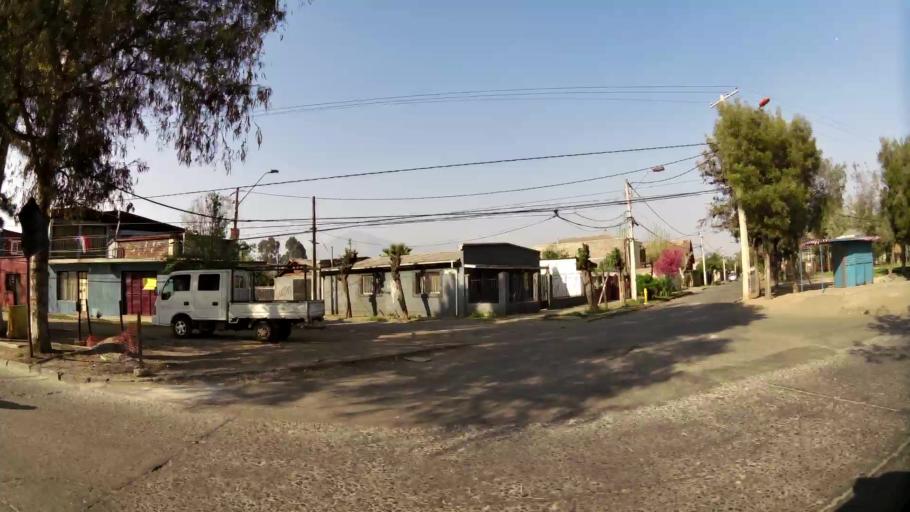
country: CL
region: Santiago Metropolitan
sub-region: Provincia de Santiago
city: Lo Prado
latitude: -33.3755
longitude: -70.6904
